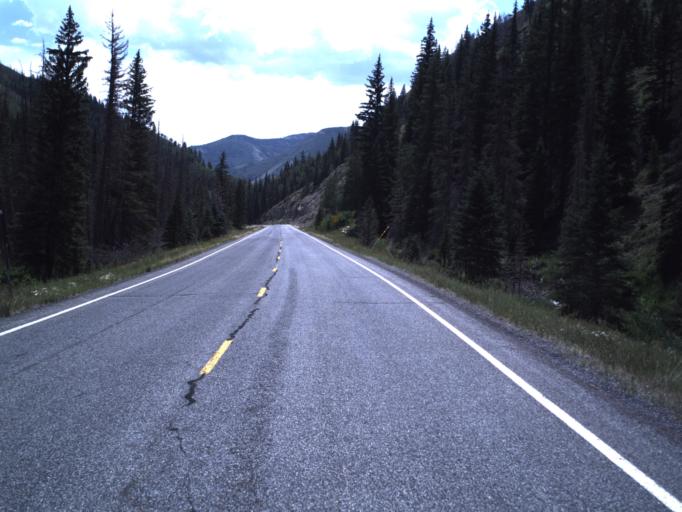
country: US
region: Utah
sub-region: Emery County
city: Huntington
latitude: 39.5119
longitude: -111.1562
